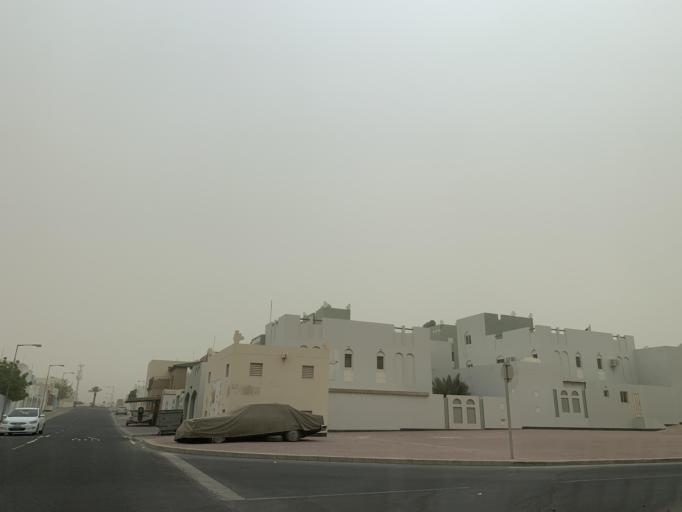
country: BH
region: Central Governorate
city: Madinat Hamad
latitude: 26.1337
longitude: 50.5114
